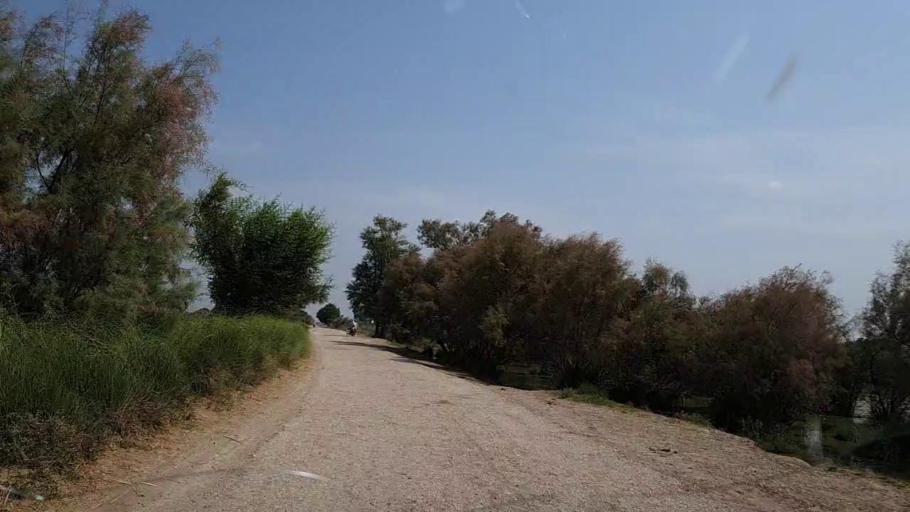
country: PK
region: Sindh
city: Khanpur
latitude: 27.8153
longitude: 69.3066
